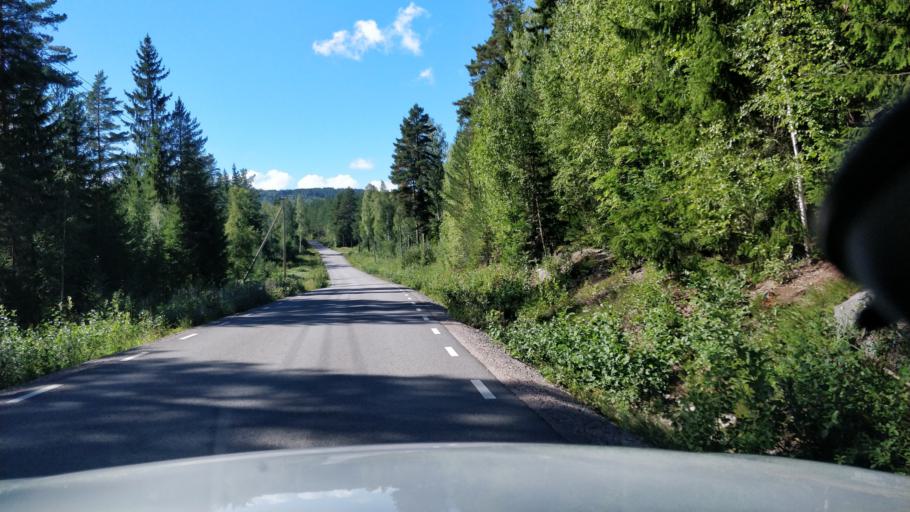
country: SE
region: Dalarna
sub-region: Faluns Kommun
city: Bjursas
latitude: 60.7514
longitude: 15.4976
